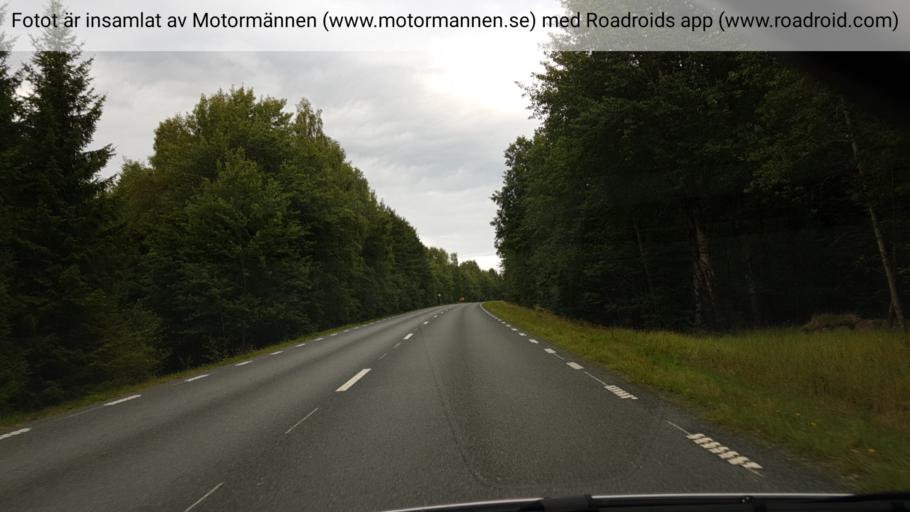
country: SE
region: Vaestra Goetaland
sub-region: Tidaholms Kommun
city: Tidaholm
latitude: 58.1907
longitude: 14.0025
